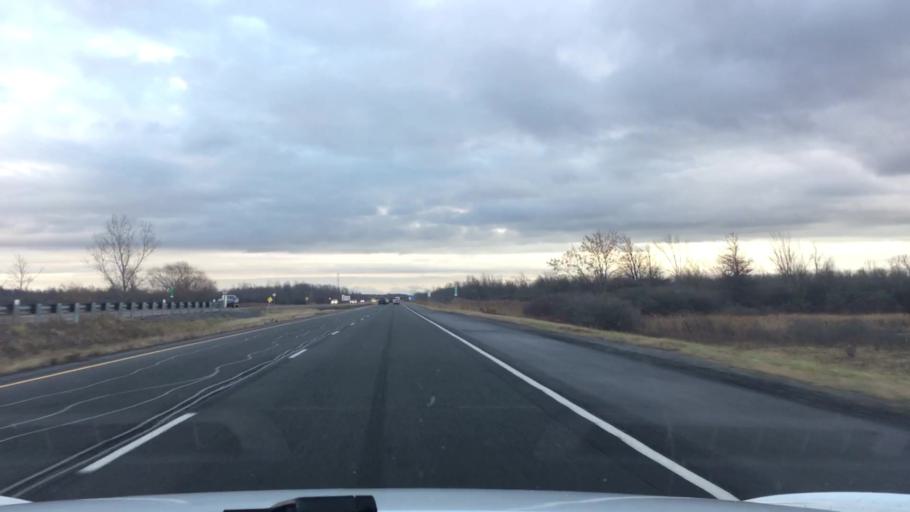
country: US
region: New York
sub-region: Erie County
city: Grandyle Village
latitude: 42.9624
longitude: -79.0211
